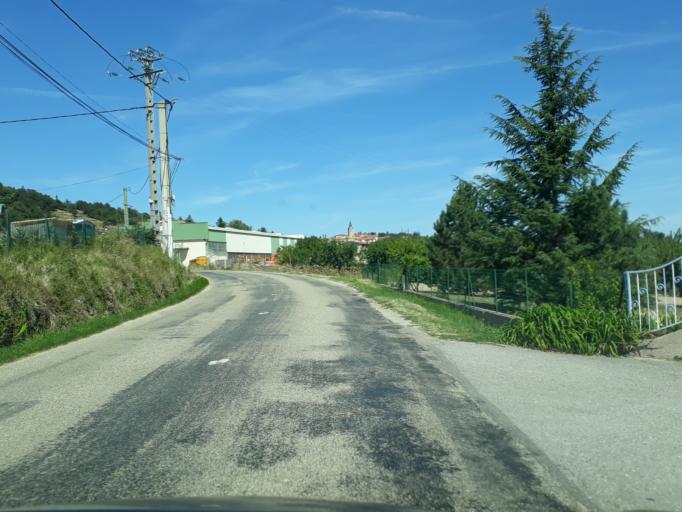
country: FR
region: Rhone-Alpes
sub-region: Departement de l'Ardeche
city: Felines
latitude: 45.3091
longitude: 4.7295
